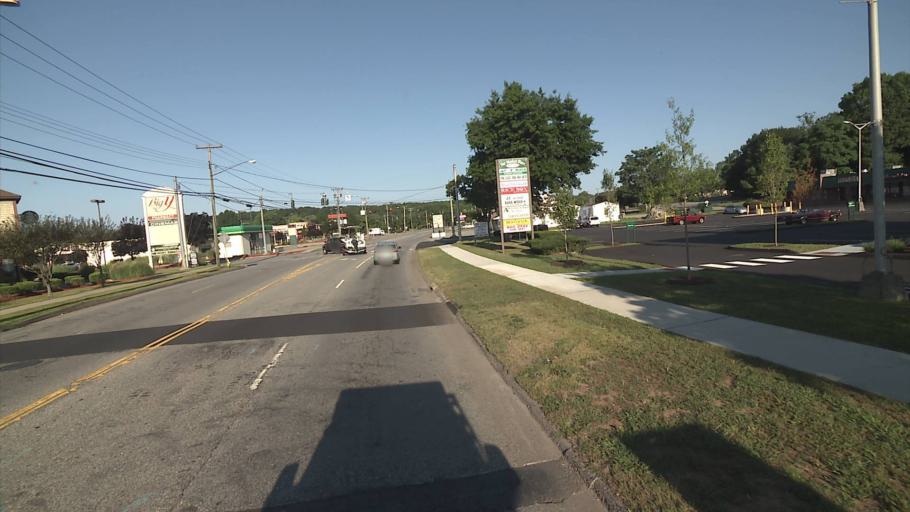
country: US
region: Connecticut
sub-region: New London County
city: Long Hill
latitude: 41.3464
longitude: -72.0485
